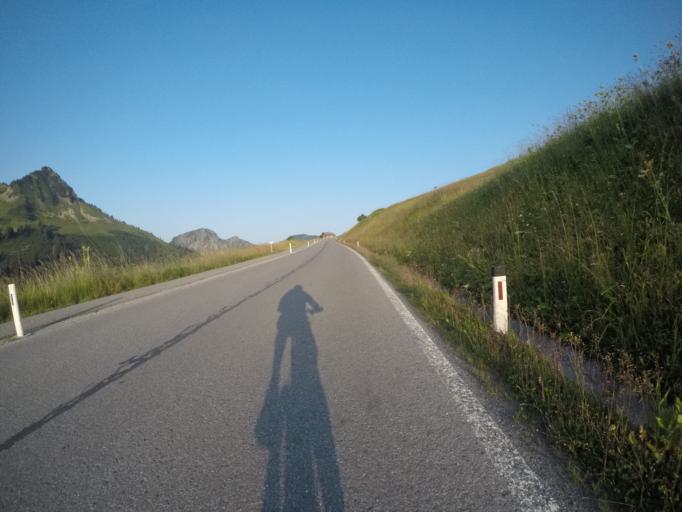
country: AT
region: Vorarlberg
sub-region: Politischer Bezirk Bregenz
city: Damuels
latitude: 47.2809
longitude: 9.8754
